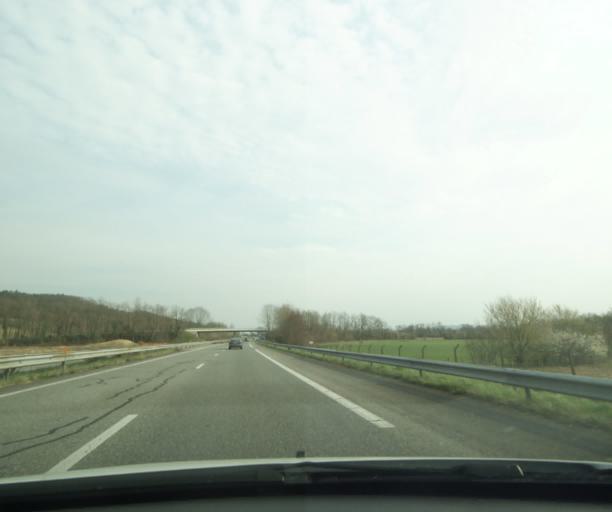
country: FR
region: Aquitaine
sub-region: Departement des Pyrenees-Atlantiques
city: Denguin
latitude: 43.3693
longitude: -0.4833
